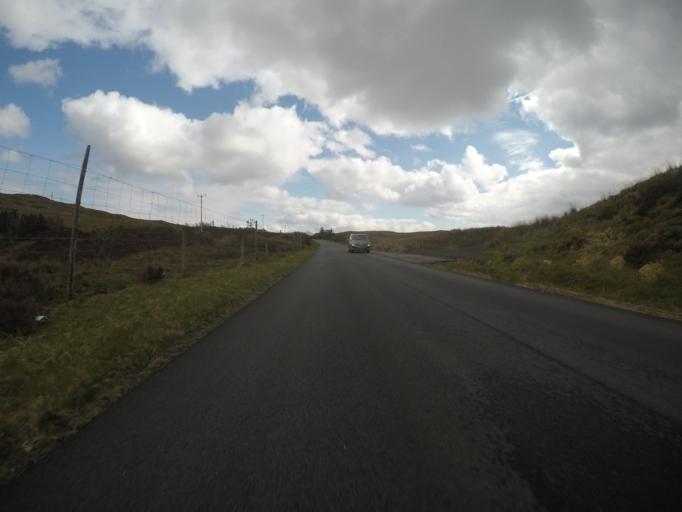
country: GB
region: Scotland
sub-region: Highland
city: Isle of Skye
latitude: 57.3351
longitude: -6.3511
